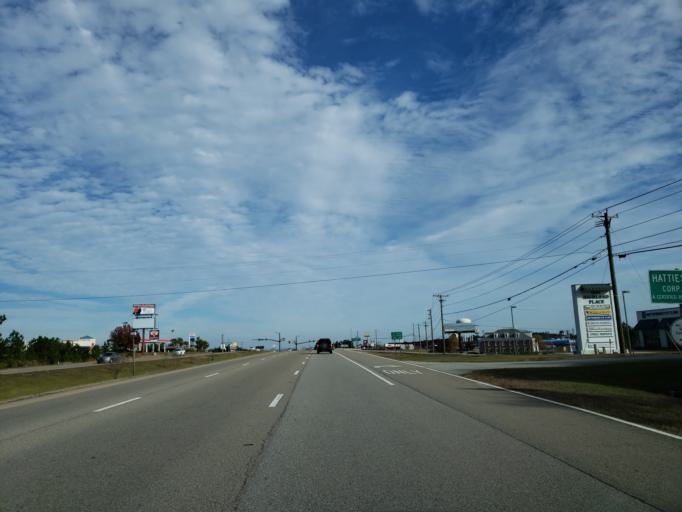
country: US
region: Mississippi
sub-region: Lamar County
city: West Hattiesburg
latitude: 31.3173
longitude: -89.4161
